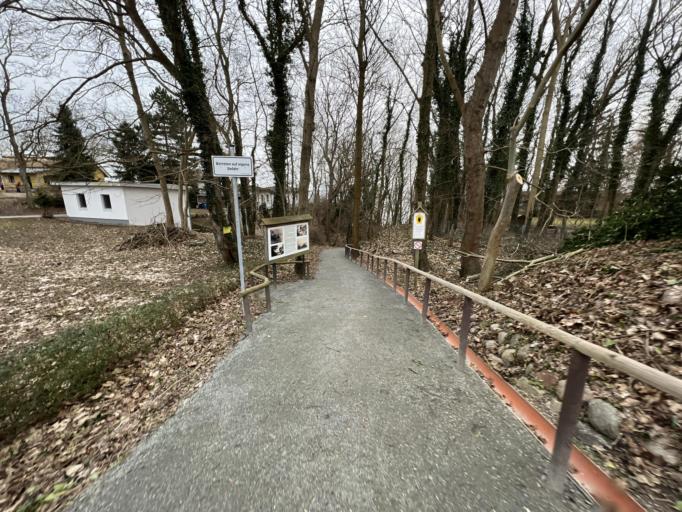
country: DE
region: Mecklenburg-Vorpommern
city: Ostseebad Gohren
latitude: 54.3394
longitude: 13.7514
